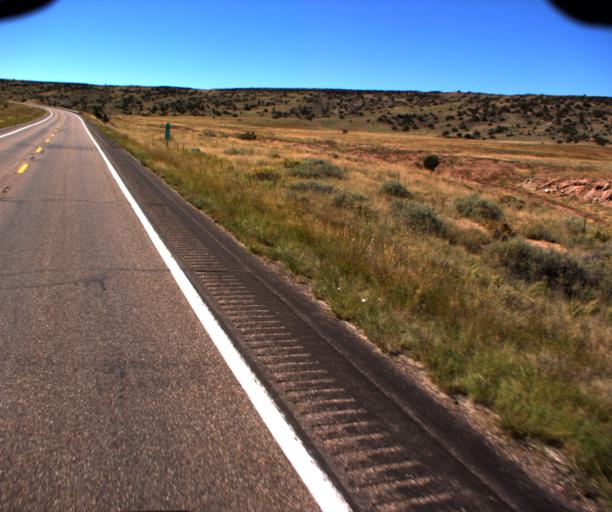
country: US
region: Arizona
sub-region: Apache County
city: Saint Johns
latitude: 34.3419
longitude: -109.3834
